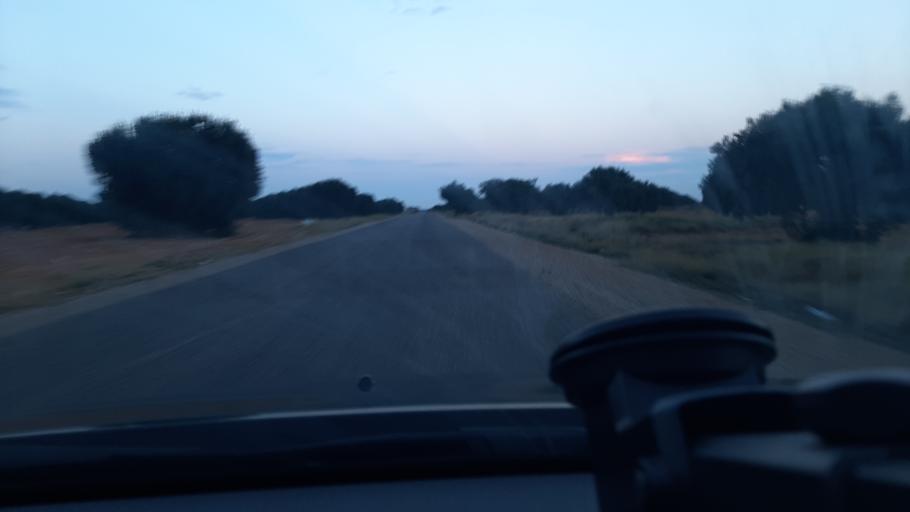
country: TN
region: Al Mahdiyah
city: Shurban
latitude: 34.9884
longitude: 10.3933
